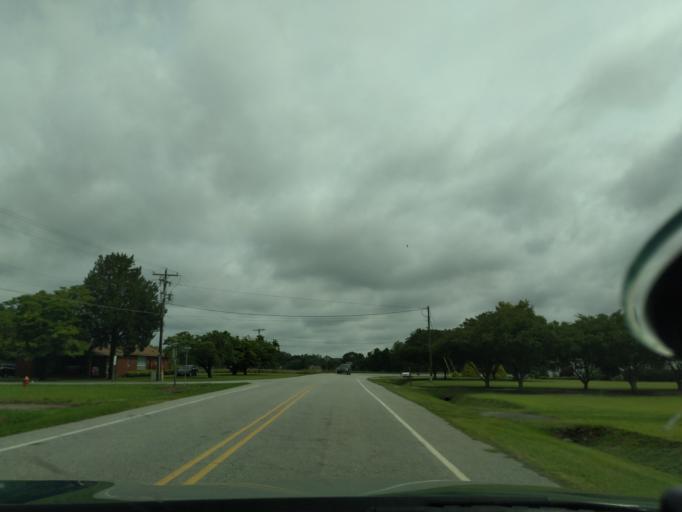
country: US
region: North Carolina
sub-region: Washington County
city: Plymouth
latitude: 35.8514
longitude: -76.7312
